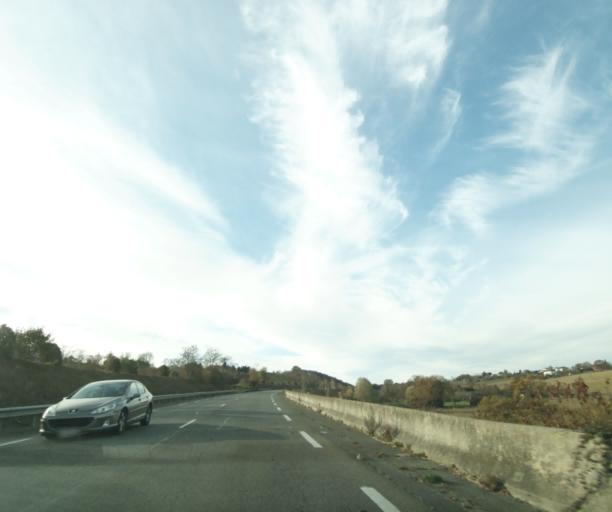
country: FR
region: Midi-Pyrenees
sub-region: Departement du Gers
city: Auch
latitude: 43.6624
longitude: 0.5888
